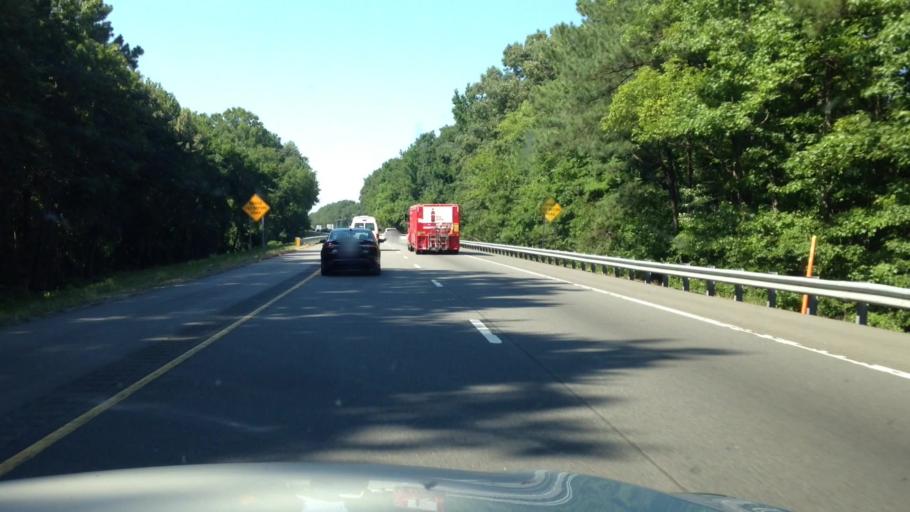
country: US
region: North Carolina
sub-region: Halifax County
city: Enfield
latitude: 36.1413
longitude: -77.7870
